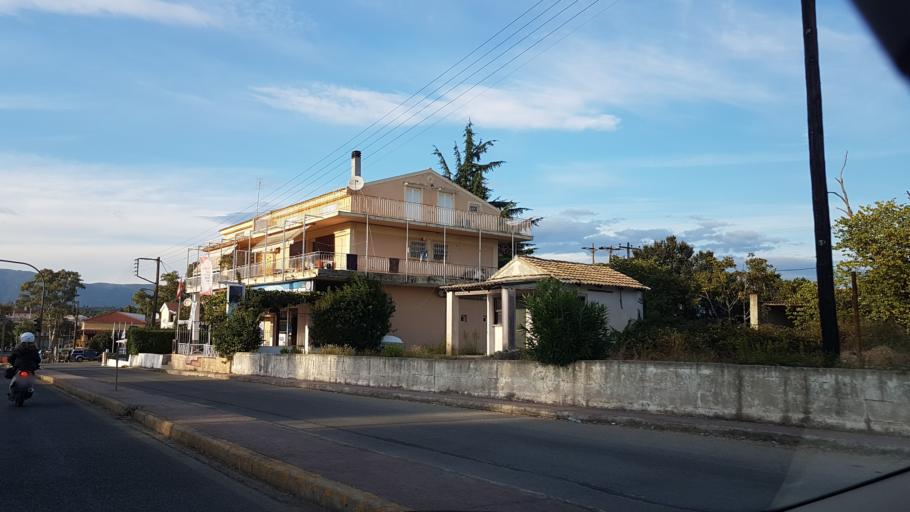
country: GR
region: Ionian Islands
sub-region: Nomos Kerkyras
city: Kontokali
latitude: 39.6574
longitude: 19.8394
